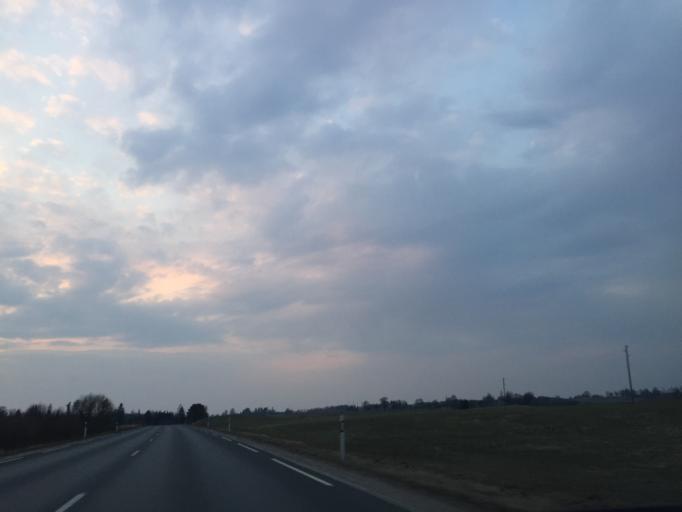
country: LV
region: Raunas
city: Rauna
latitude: 57.2600
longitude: 25.5334
